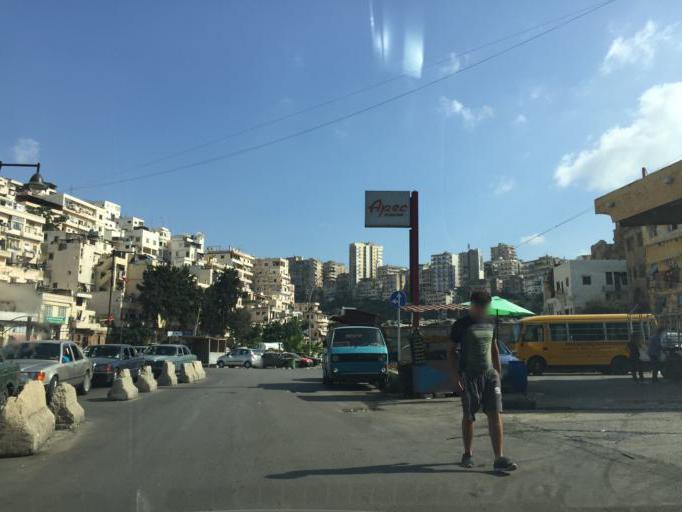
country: LB
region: Liban-Nord
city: Tripoli
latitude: 34.4348
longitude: 35.8459
